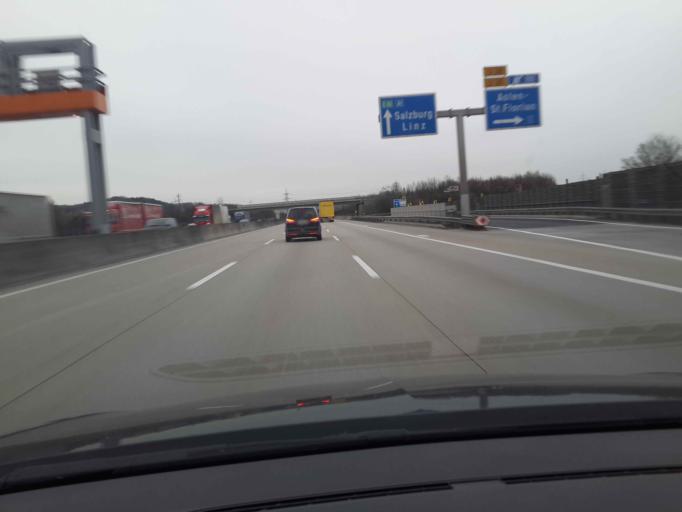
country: AT
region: Upper Austria
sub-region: Politischer Bezirk Linz-Land
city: Asten
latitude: 48.2170
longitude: 14.4109
